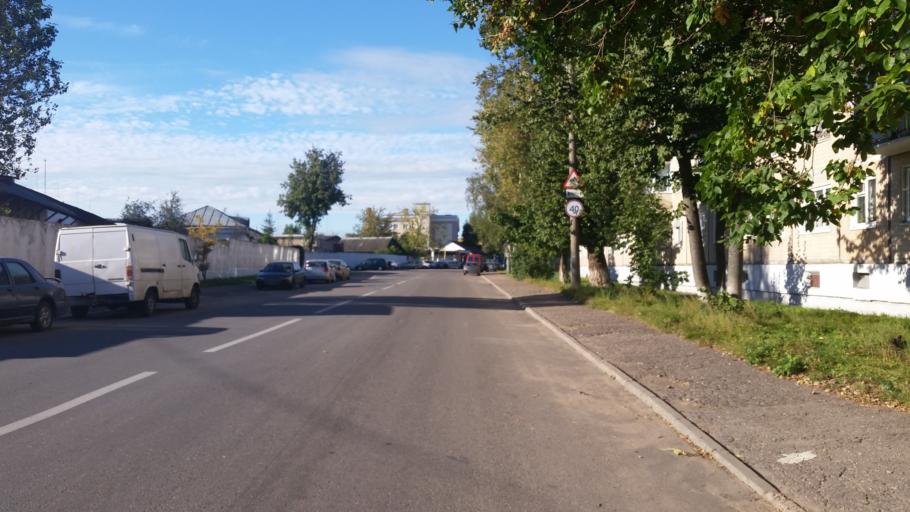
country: BY
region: Vitebsk
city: Vitebsk
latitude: 55.1784
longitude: 30.1876
